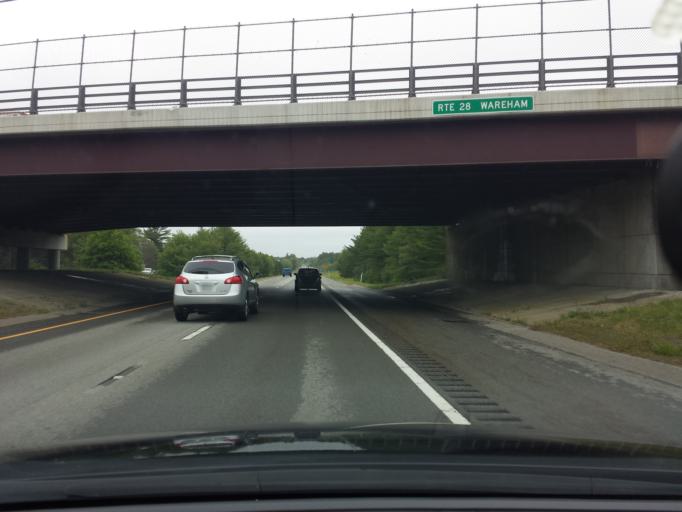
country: US
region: Massachusetts
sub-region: Plymouth County
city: Wareham Center
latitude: 41.7749
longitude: -70.7392
